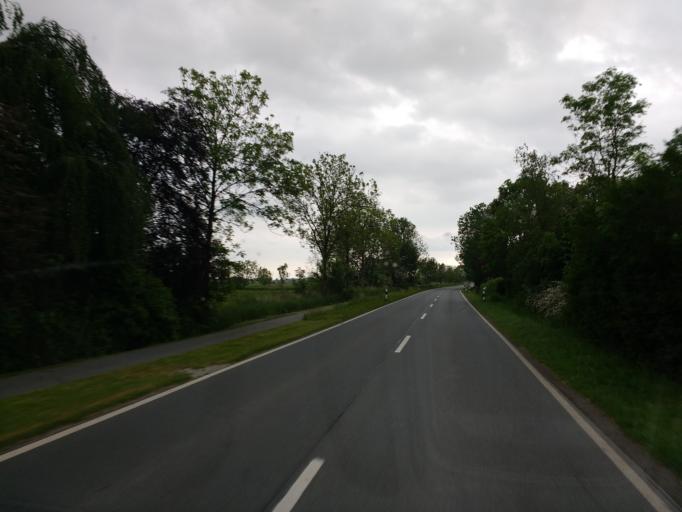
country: DE
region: Lower Saxony
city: Schillig
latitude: 53.6528
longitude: 7.9926
